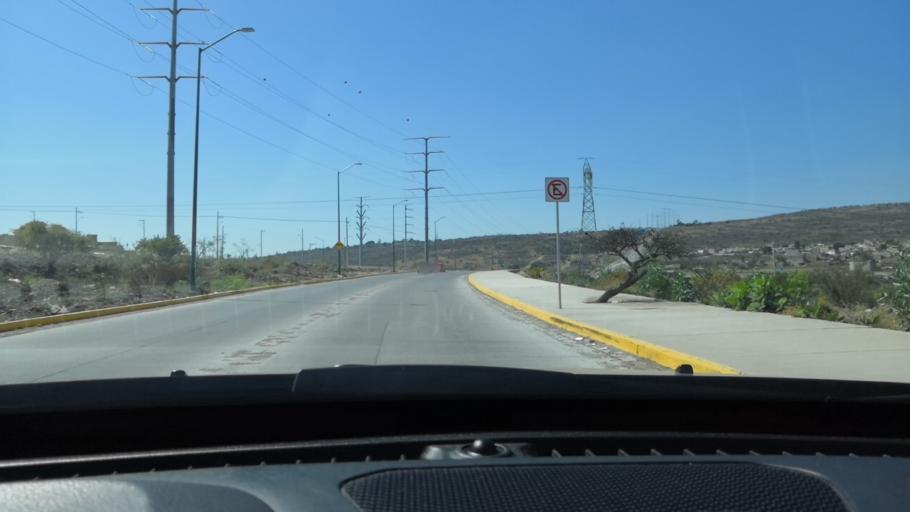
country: MX
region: Guanajuato
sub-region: Leon
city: Ejido la Joya
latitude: 21.1278
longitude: -101.7348
